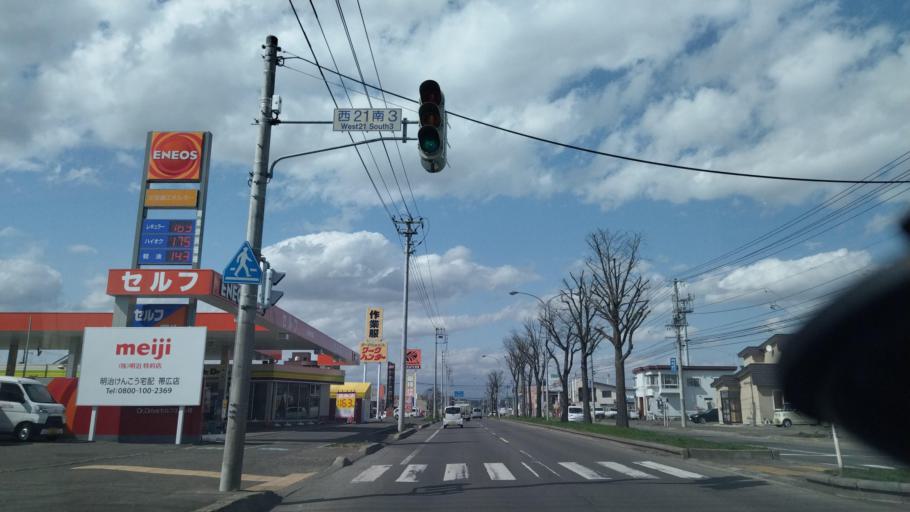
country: JP
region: Hokkaido
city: Obihiro
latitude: 42.9152
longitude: 143.1448
